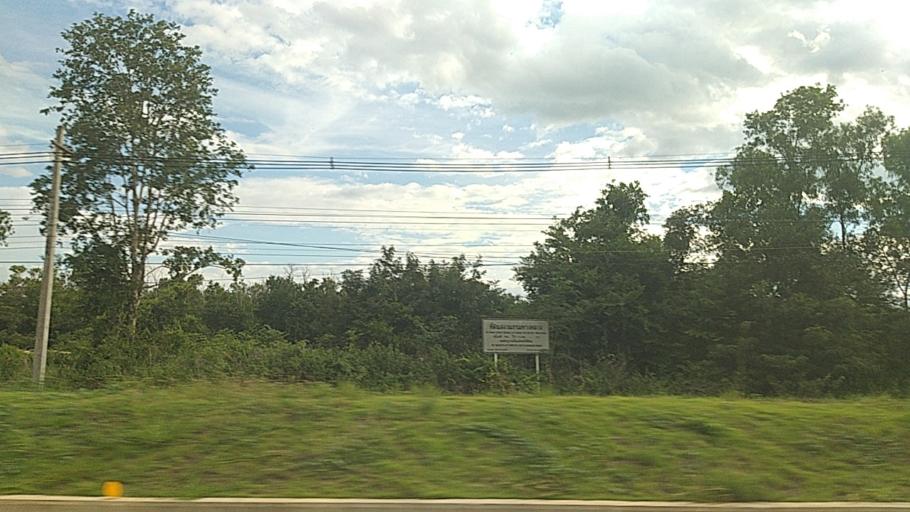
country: TH
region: Surin
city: Kap Choeng
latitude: 14.5360
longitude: 103.5253
